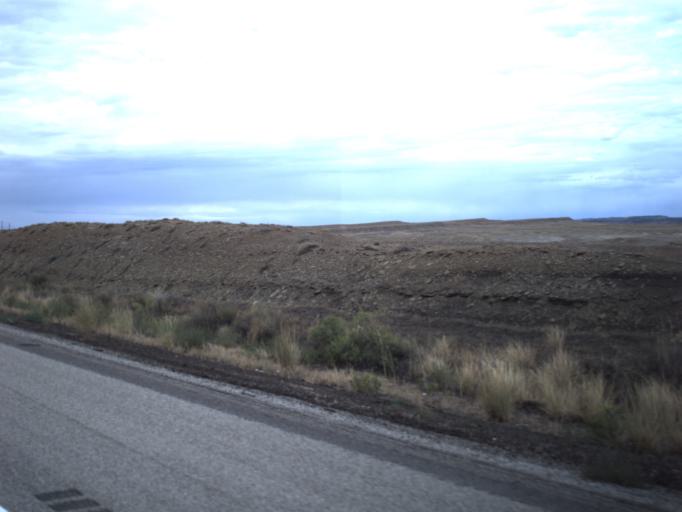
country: US
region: Colorado
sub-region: Mesa County
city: Loma
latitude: 39.0277
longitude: -109.2921
